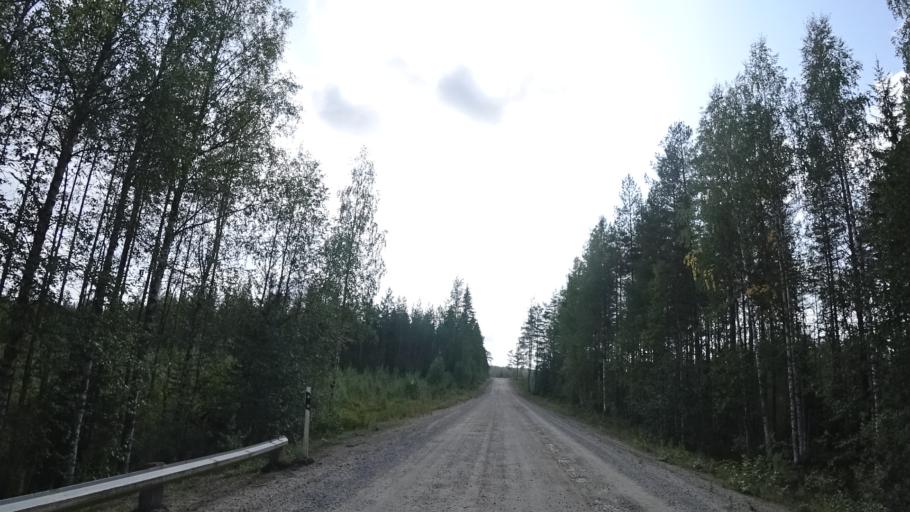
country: FI
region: North Karelia
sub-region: Pielisen Karjala
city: Lieksa
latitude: 63.5754
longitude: 30.1214
